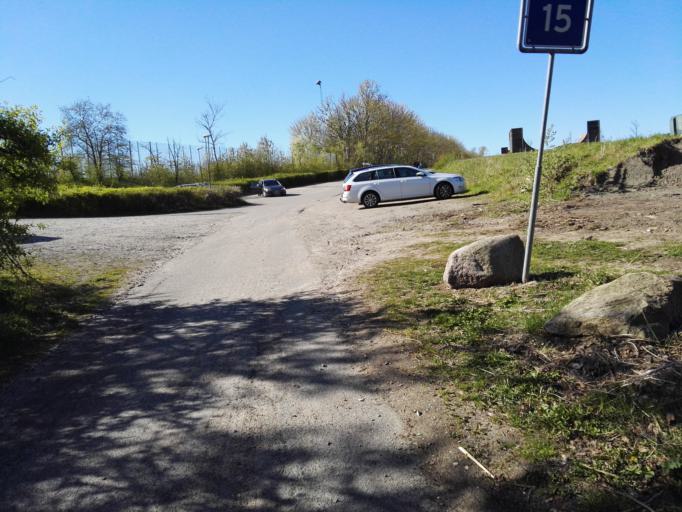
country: DK
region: Capital Region
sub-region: Egedal Kommune
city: Stenlose
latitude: 55.7609
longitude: 12.2010
